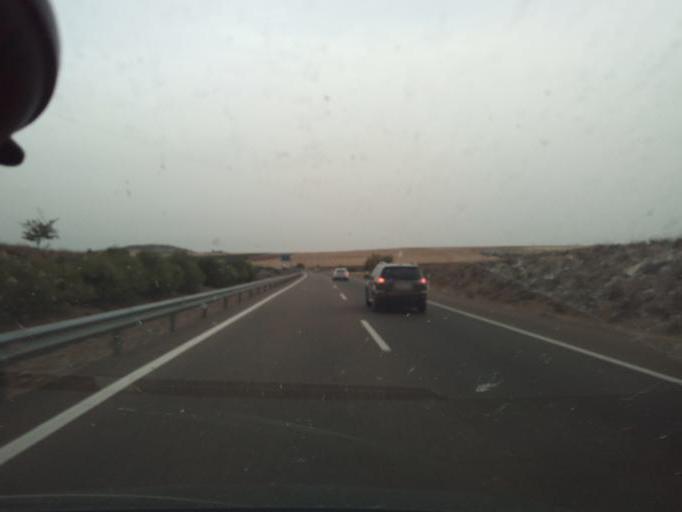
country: ES
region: Extremadura
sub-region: Provincia de Badajoz
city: Merida
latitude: 38.9460
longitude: -6.3136
